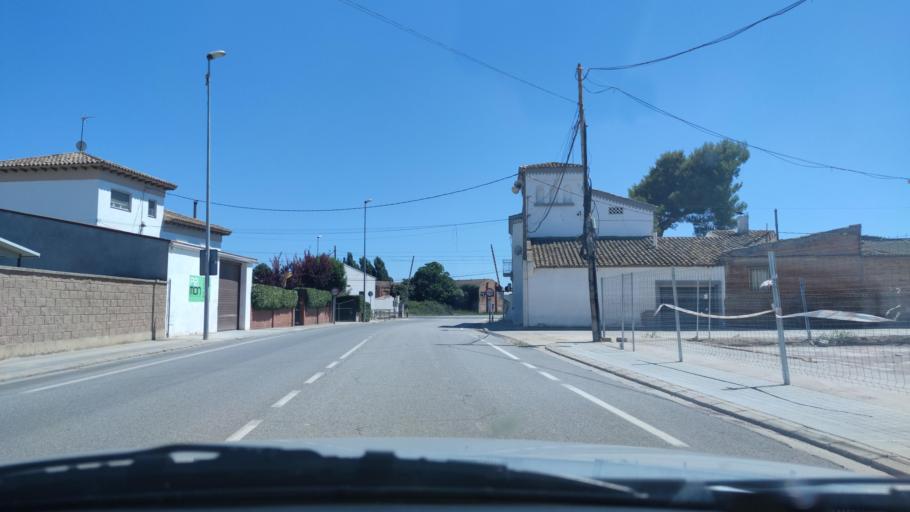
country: ES
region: Catalonia
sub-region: Provincia de Lleida
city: Mollerussa
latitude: 41.6324
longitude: 0.8767
